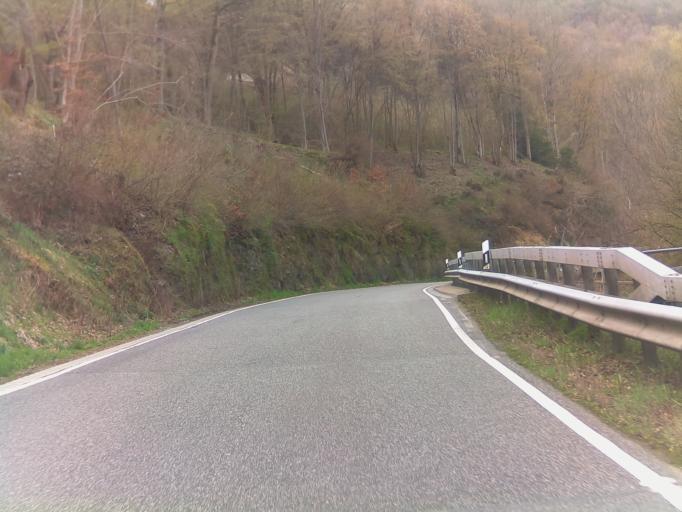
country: DE
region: Rheinland-Pfalz
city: Heinzenberg
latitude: 49.8301
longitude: 7.4849
